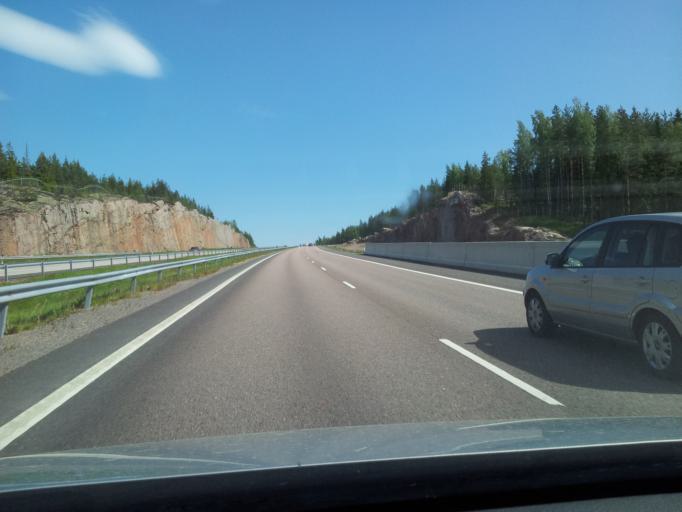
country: FI
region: Uusimaa
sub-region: Loviisa
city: Perna
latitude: 60.4872
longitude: 26.0129
